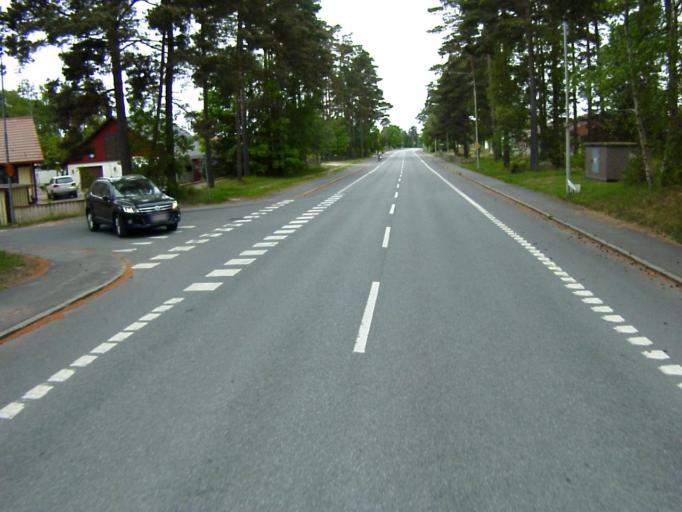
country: SE
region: Skane
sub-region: Kristianstads Kommun
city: Ahus
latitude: 55.9395
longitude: 14.2946
